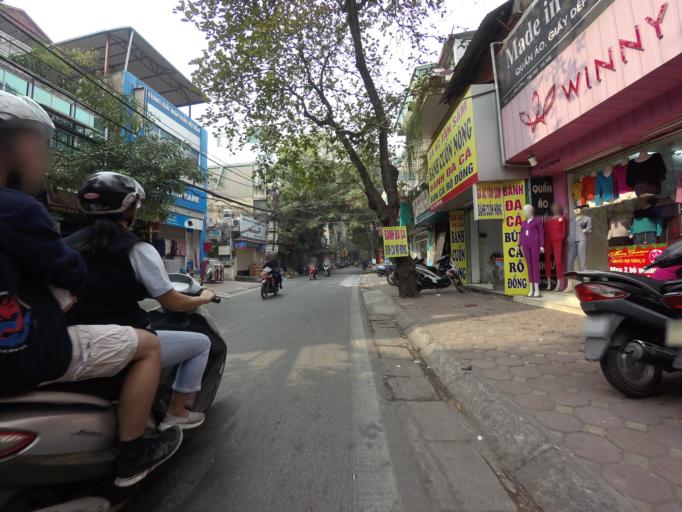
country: VN
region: Ha Noi
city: Hoan Kiem
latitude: 21.0529
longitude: 105.8367
